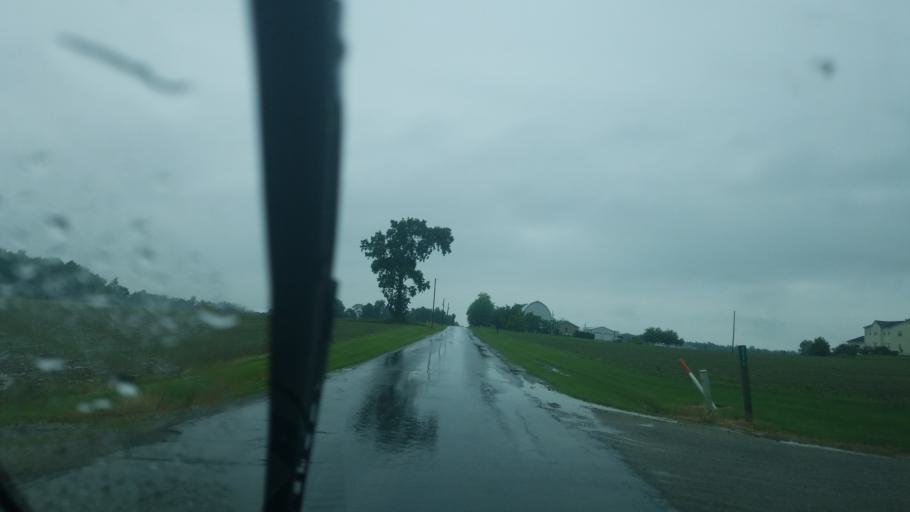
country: US
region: Ohio
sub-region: Huron County
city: Plymouth
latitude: 40.9863
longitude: -82.6054
